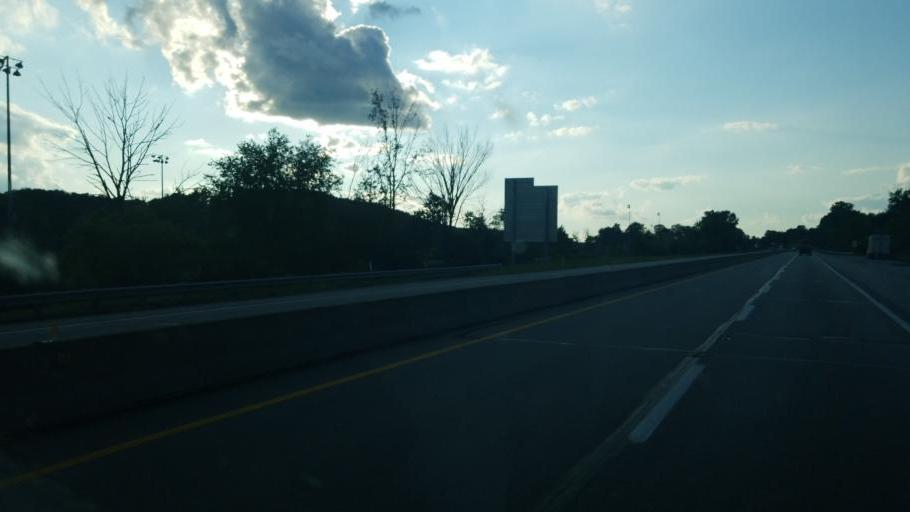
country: US
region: Pennsylvania
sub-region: Butler County
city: Fernway
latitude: 40.7124
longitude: -80.1305
